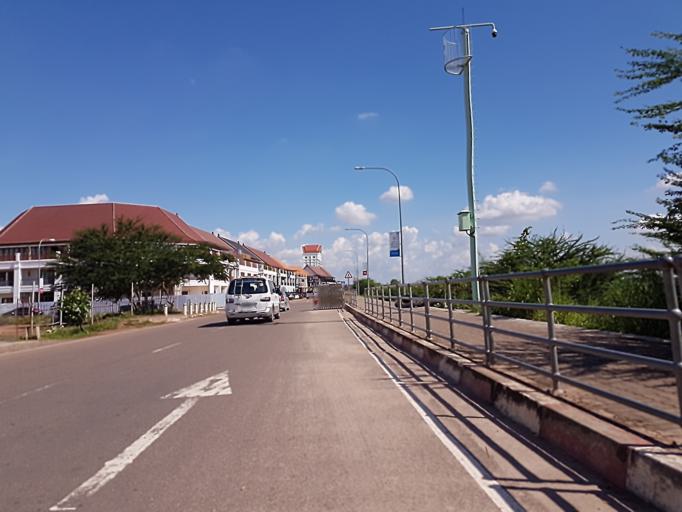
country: LA
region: Vientiane
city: Vientiane
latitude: 17.9596
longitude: 102.6091
